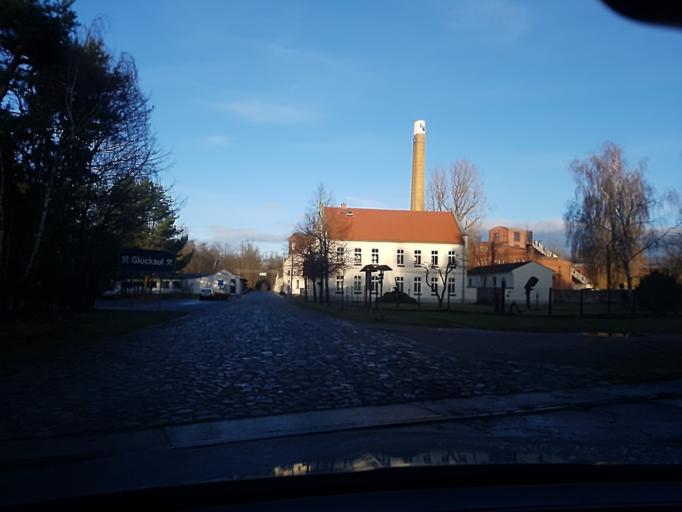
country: DE
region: Brandenburg
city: Trobitz
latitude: 51.5825
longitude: 13.4150
